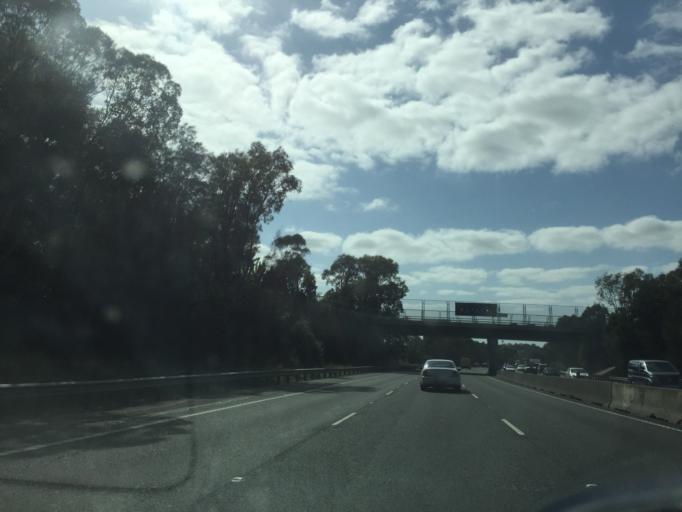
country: AU
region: New South Wales
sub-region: Holroyd
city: Girraween
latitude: -33.8063
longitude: 150.9266
